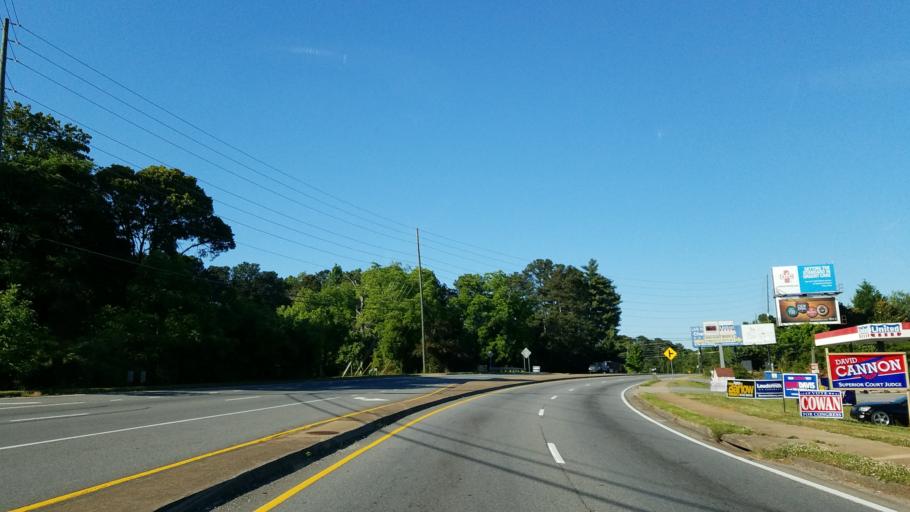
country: US
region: Georgia
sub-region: Cherokee County
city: Woodstock
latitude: 34.0964
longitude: -84.5829
